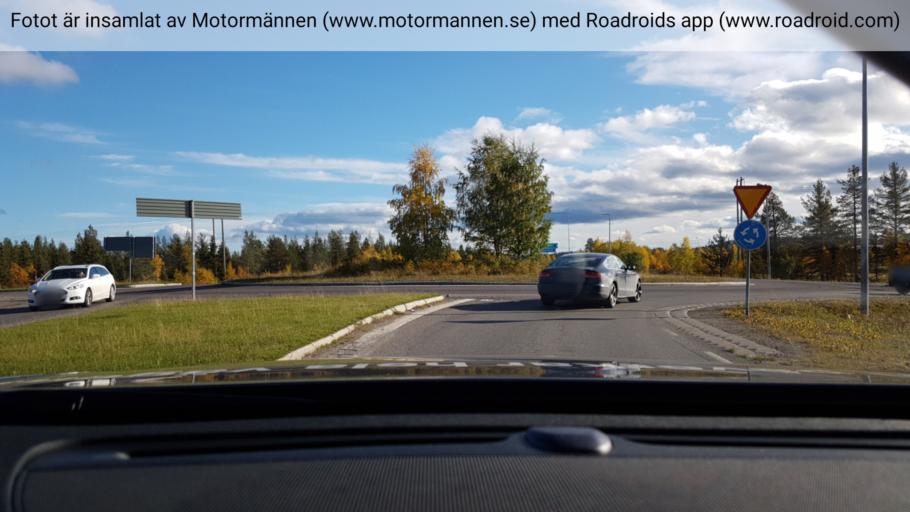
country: SE
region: Norrbotten
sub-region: Gallivare Kommun
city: Malmberget
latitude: 67.1615
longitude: 20.6551
